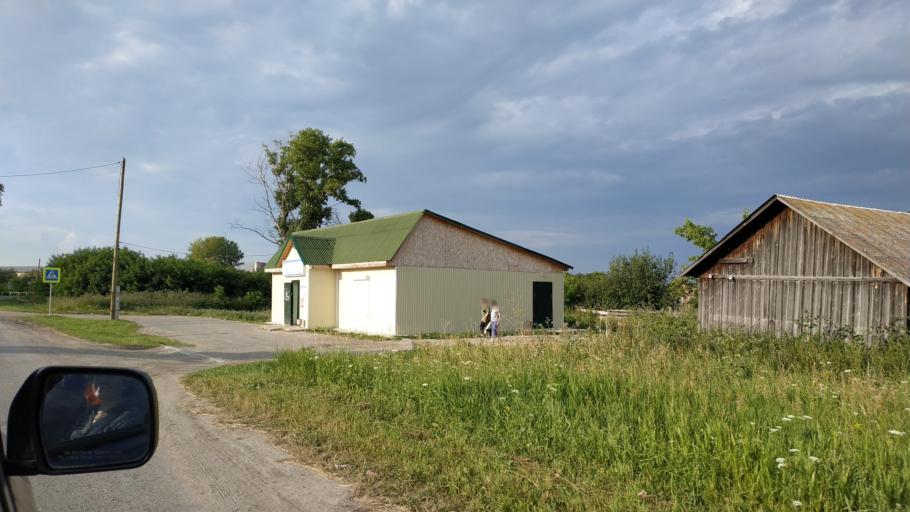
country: RU
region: Sverdlovsk
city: Yelanskiy
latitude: 57.0833
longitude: 62.4752
